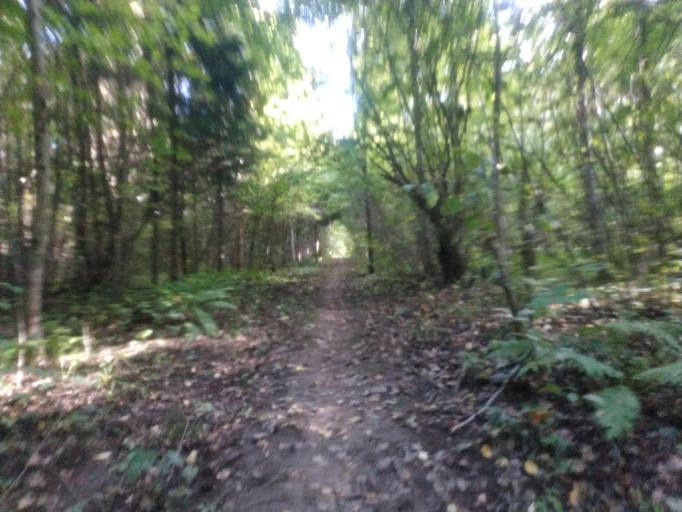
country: RU
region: Chuvashia
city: Novyye Lapsary
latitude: 56.1332
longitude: 47.1116
